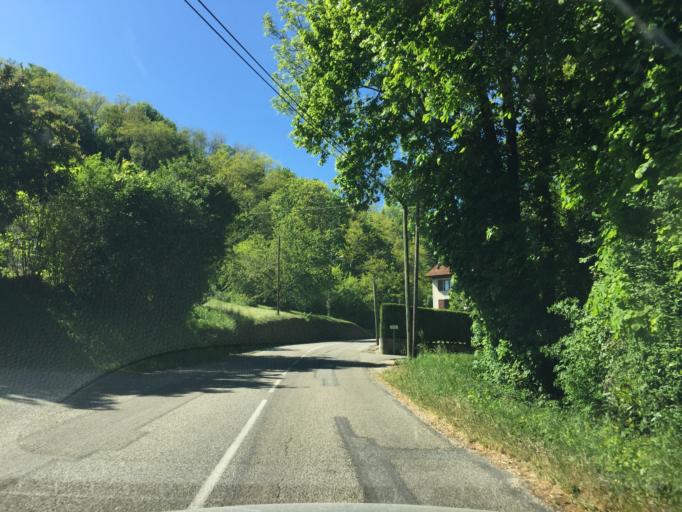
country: FR
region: Rhone-Alpes
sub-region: Departement de la Savoie
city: Cognin
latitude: 45.5658
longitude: 5.8875
